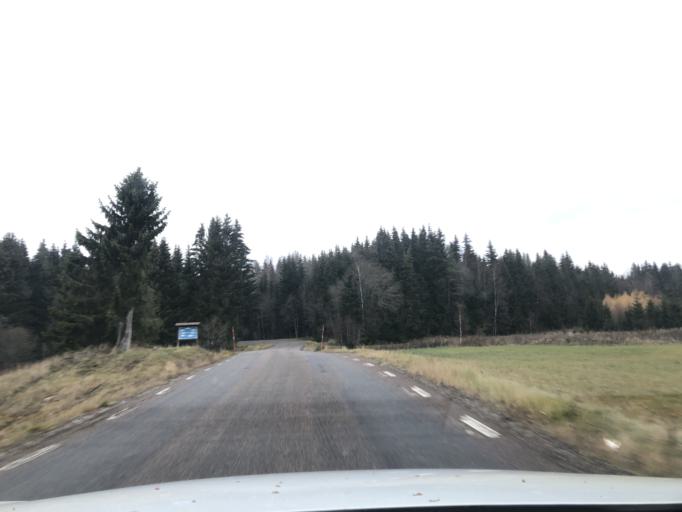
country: SE
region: Vaestra Goetaland
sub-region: Ulricehamns Kommun
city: Ulricehamn
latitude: 57.8681
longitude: 13.5477
